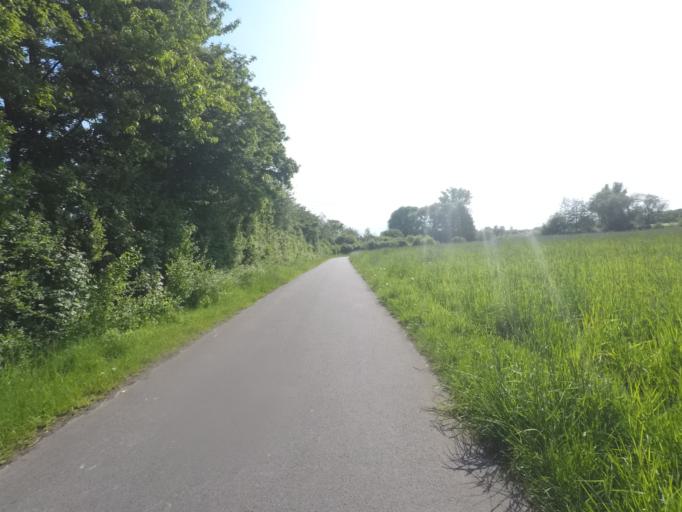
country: DE
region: North Rhine-Westphalia
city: Loehne
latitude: 52.1943
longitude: 8.6932
